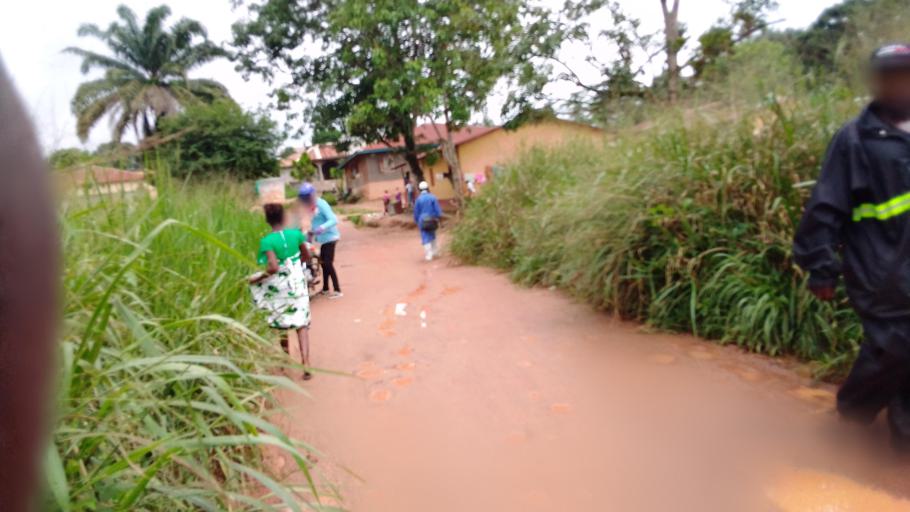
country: SL
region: Eastern Province
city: Kenema
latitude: 7.8678
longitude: -11.1804
